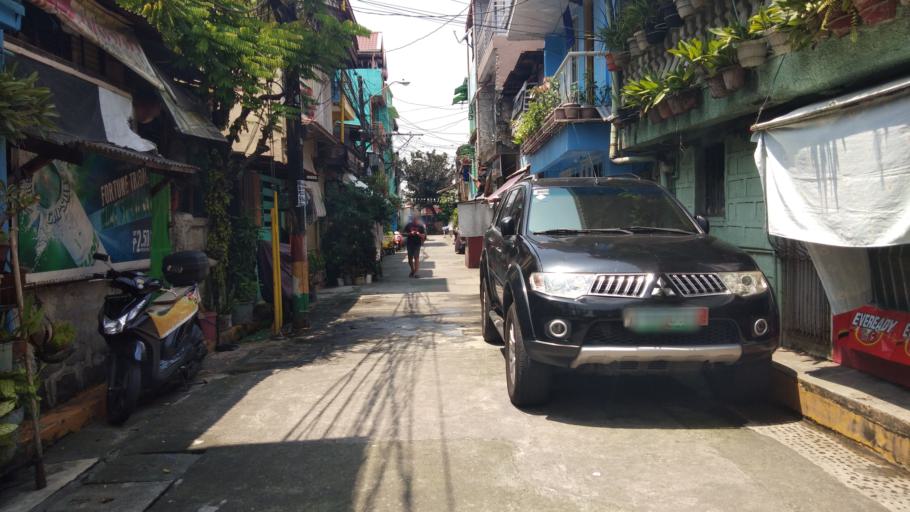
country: PH
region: Metro Manila
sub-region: San Juan
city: San Juan
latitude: 14.5876
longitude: 121.0128
